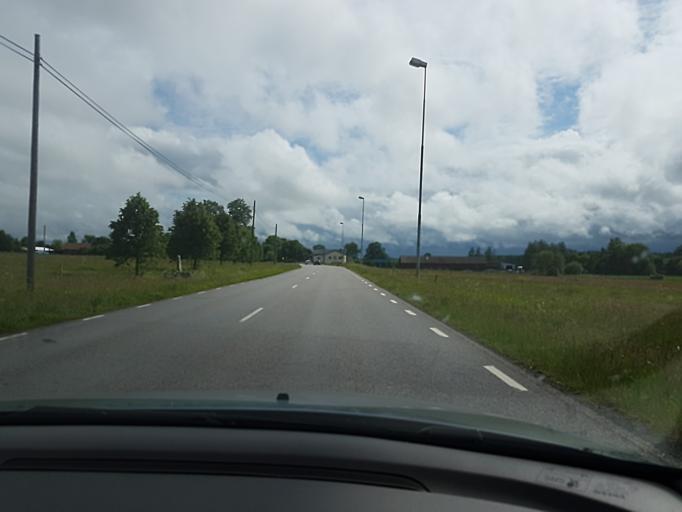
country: SE
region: Uppsala
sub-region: Osthammars Kommun
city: OEsthammar
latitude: 60.2909
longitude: 18.2849
